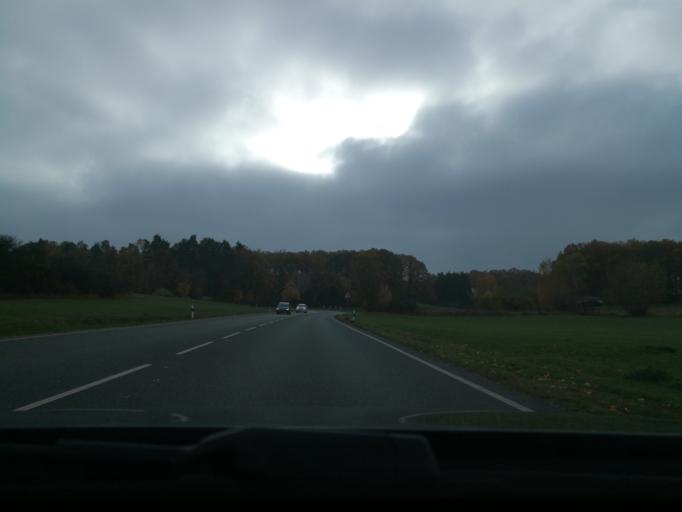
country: DE
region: Bavaria
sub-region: Regierungsbezirk Mittelfranken
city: Veitsbronn
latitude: 49.5029
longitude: 10.8932
